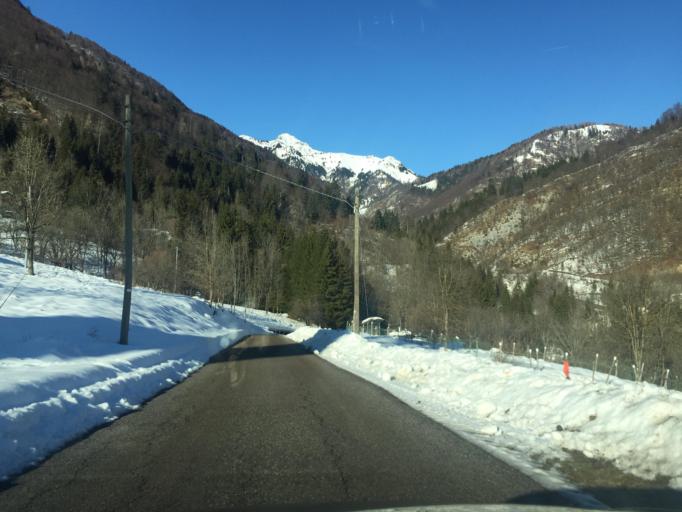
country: IT
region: Friuli Venezia Giulia
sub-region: Provincia di Udine
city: Lauco
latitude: 46.4408
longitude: 12.9494
